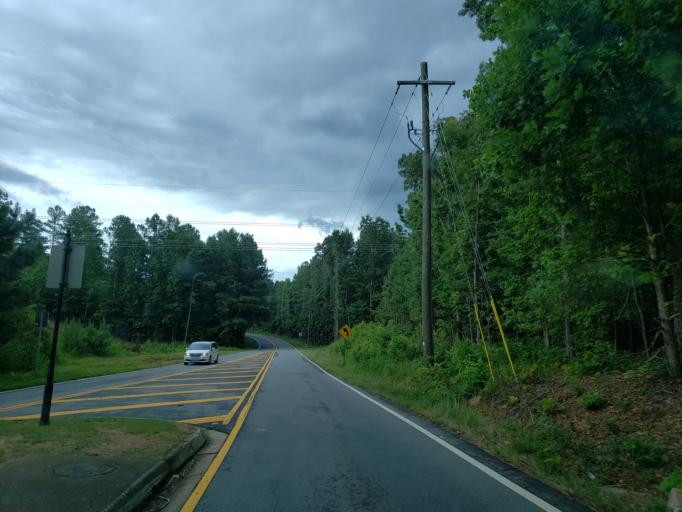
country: US
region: Georgia
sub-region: Paulding County
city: Dallas
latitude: 34.0064
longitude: -84.8029
